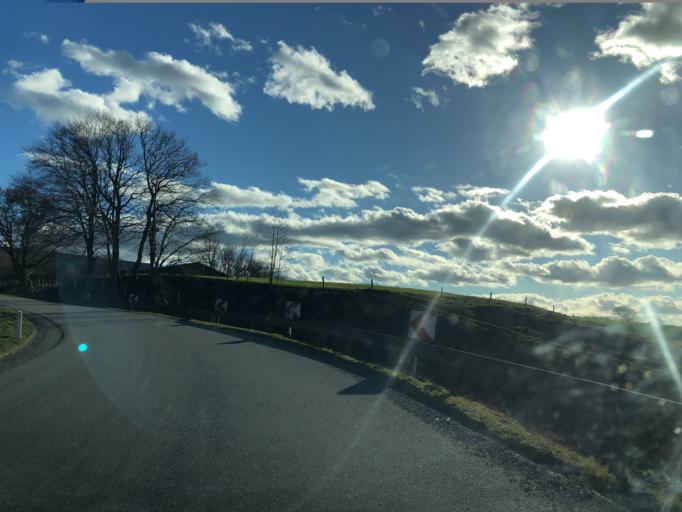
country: DK
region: Central Jutland
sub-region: Silkeborg Kommune
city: Kjellerup
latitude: 56.3241
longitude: 9.4759
